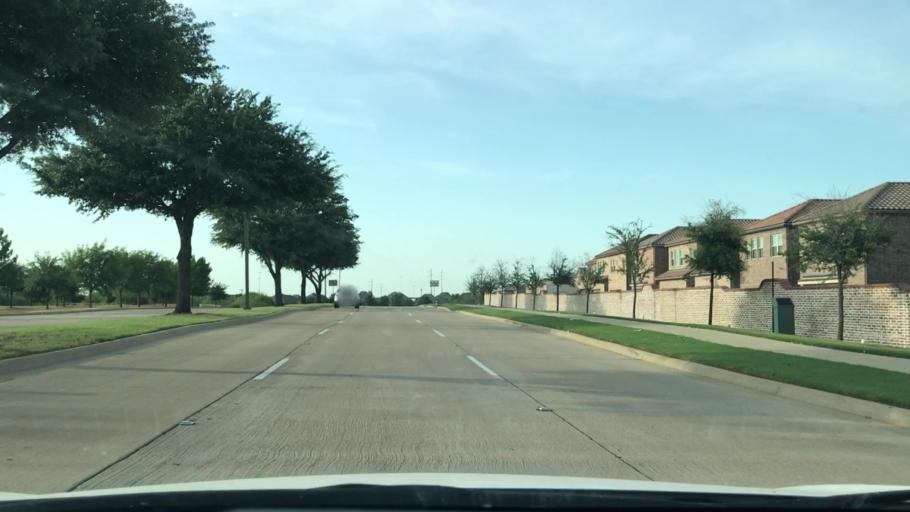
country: US
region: Texas
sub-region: Dallas County
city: Farmers Branch
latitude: 32.8997
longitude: -96.9453
